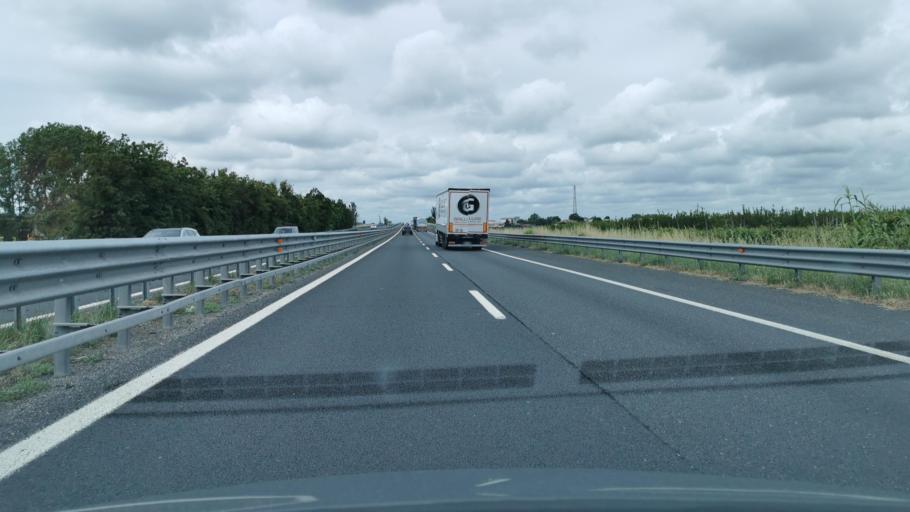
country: IT
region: Emilia-Romagna
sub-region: Provincia di Ravenna
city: Bagnacavallo
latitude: 44.4073
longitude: 12.0088
